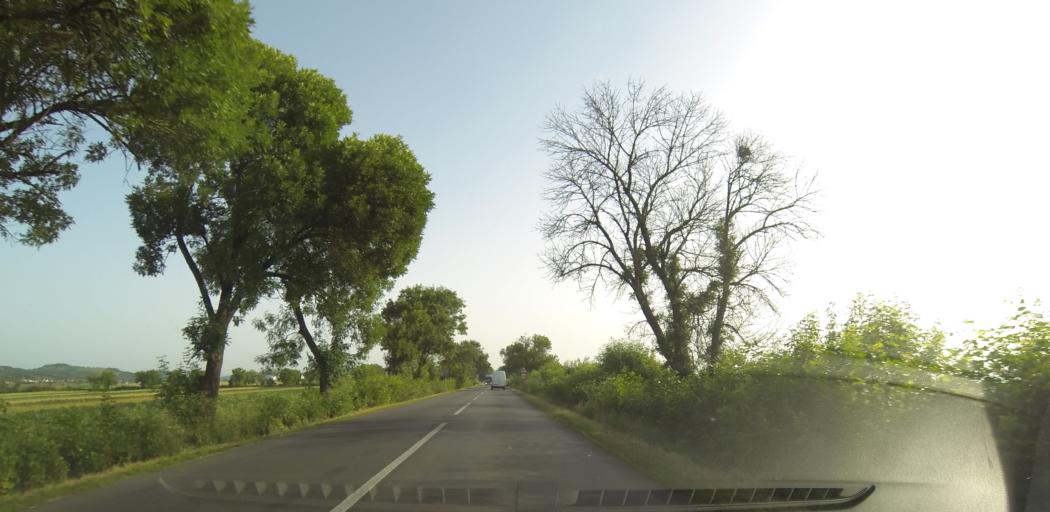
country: RO
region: Valcea
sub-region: Comuna Orlesti
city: Orlesti
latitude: 44.7790
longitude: 24.2444
